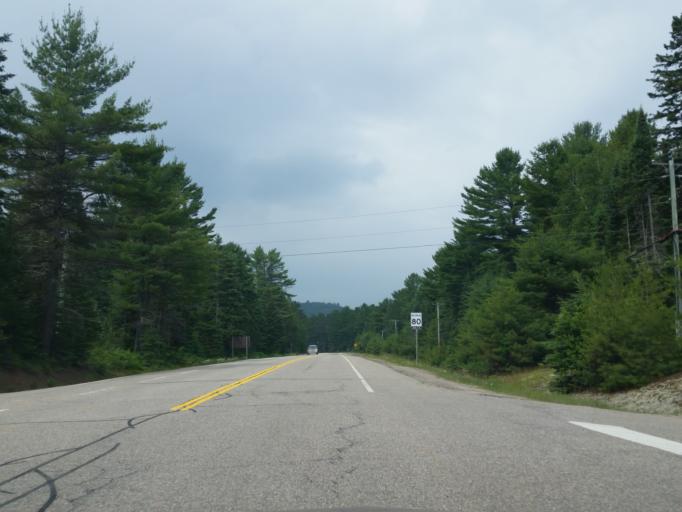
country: CA
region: Ontario
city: Huntsville
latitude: 45.5789
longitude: -78.5157
